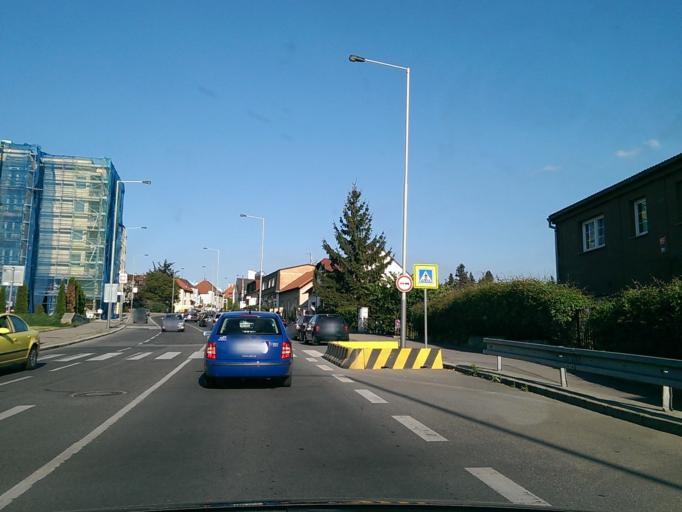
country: CZ
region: Praha
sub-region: Praha 14
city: Hostavice
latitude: 50.0521
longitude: 14.5310
